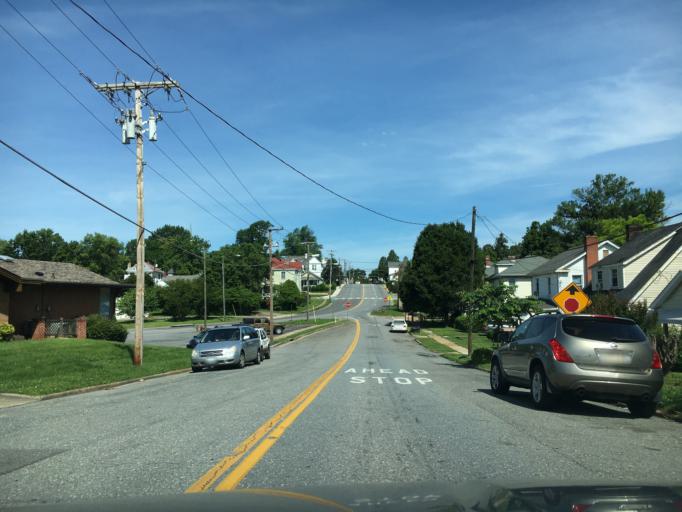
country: US
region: Virginia
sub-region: City of Lynchburg
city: West Lynchburg
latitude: 37.3963
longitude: -79.1666
